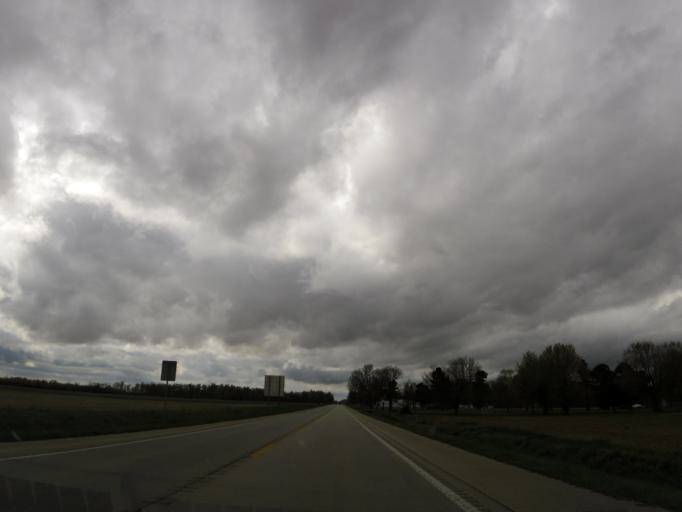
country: US
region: Missouri
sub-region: Butler County
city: Poplar Bluff
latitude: 36.6462
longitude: -90.5203
